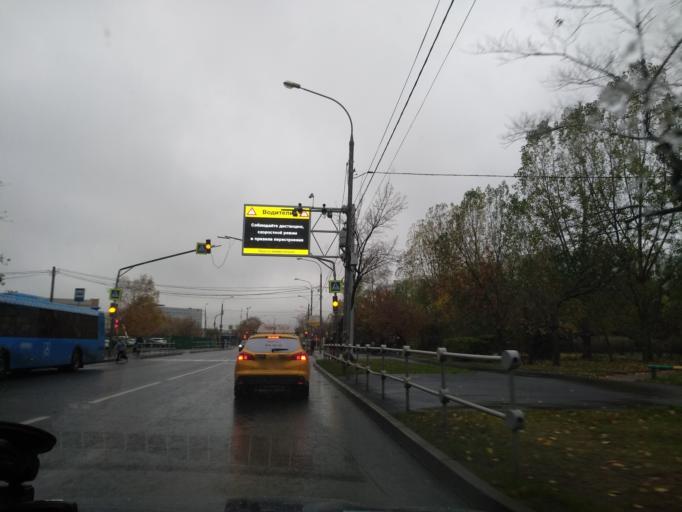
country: RU
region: Moscow
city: Slobodka
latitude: 55.8686
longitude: 37.5911
